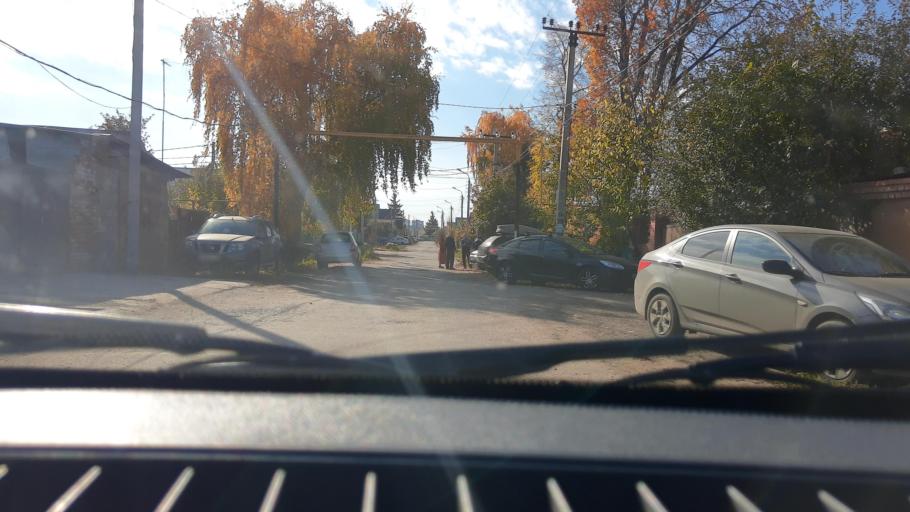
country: RU
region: Bashkortostan
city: Ufa
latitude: 54.7805
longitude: 56.0648
